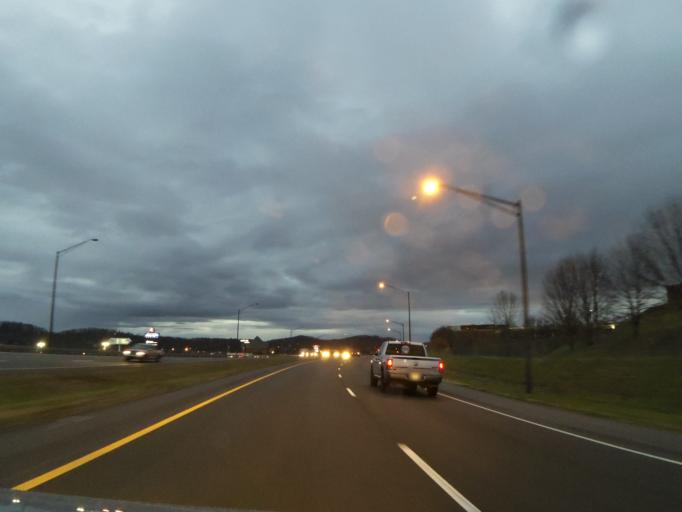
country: US
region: Tennessee
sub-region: Washington County
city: Midway
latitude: 36.3386
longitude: -82.4058
